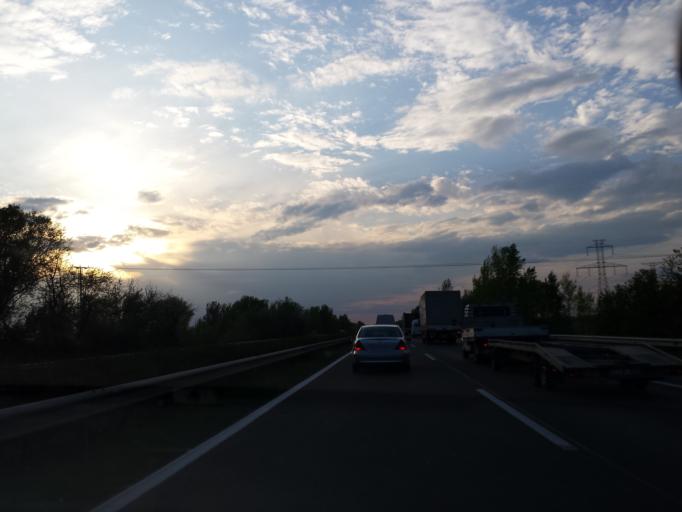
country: HU
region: Gyor-Moson-Sopron
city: Abda
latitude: 47.6603
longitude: 17.5858
